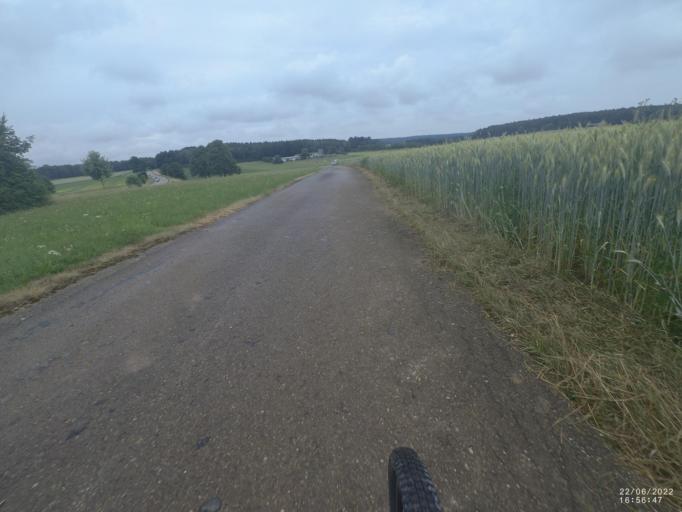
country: DE
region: Baden-Wuerttemberg
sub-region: Regierungsbezirk Stuttgart
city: Gerstetten
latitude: 48.6329
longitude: 10.0288
